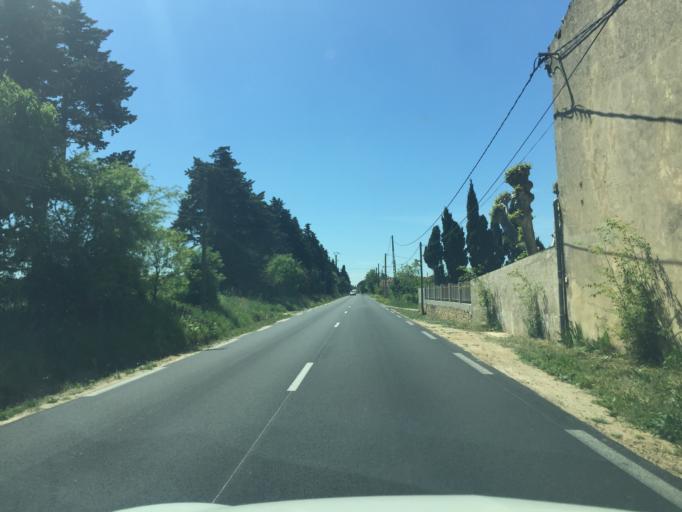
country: FR
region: Provence-Alpes-Cote d'Azur
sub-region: Departement du Vaucluse
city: Orange
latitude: 44.1163
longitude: 4.7959
